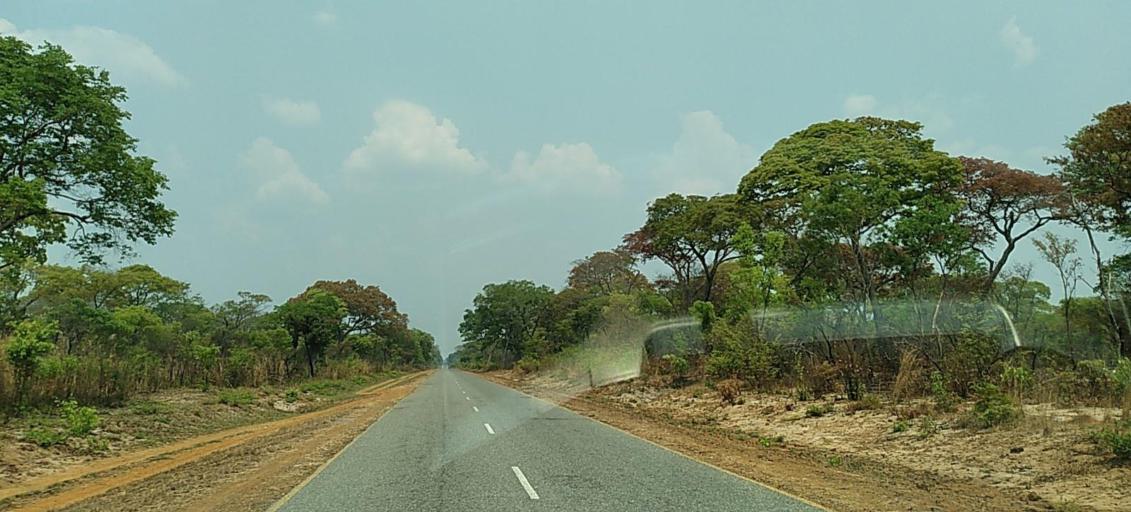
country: ZM
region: North-Western
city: Zambezi
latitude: -13.5624
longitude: 23.2160
